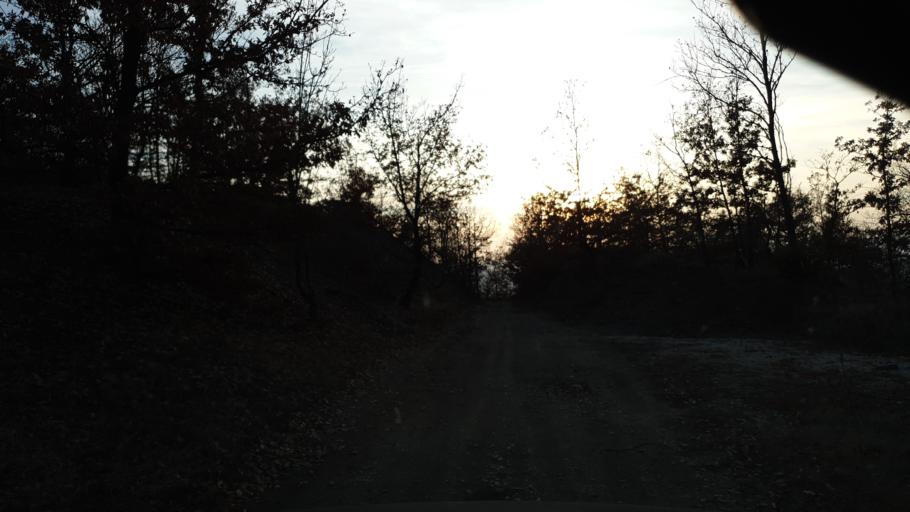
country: RS
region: Central Serbia
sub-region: Borski Okrug
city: Bor
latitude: 44.0702
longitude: 22.0754
